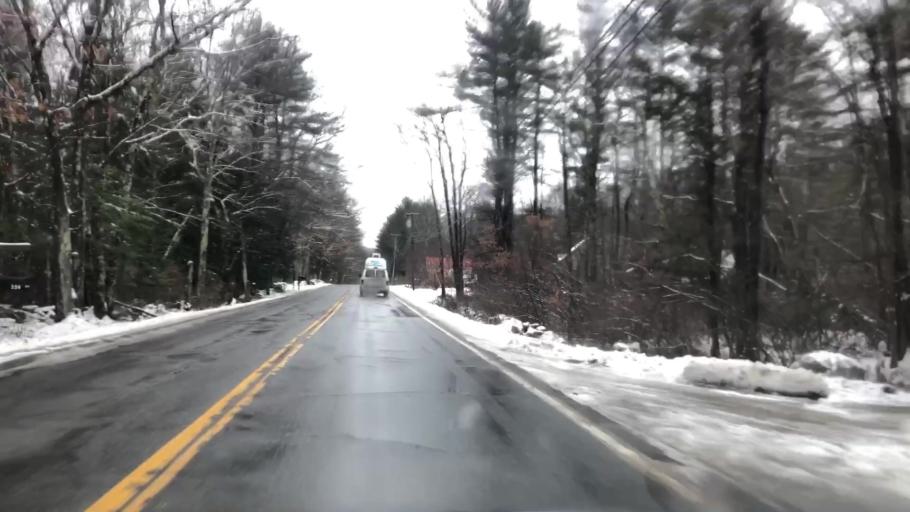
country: US
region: New Hampshire
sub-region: Hillsborough County
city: Weare
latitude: 43.0439
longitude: -71.7070
